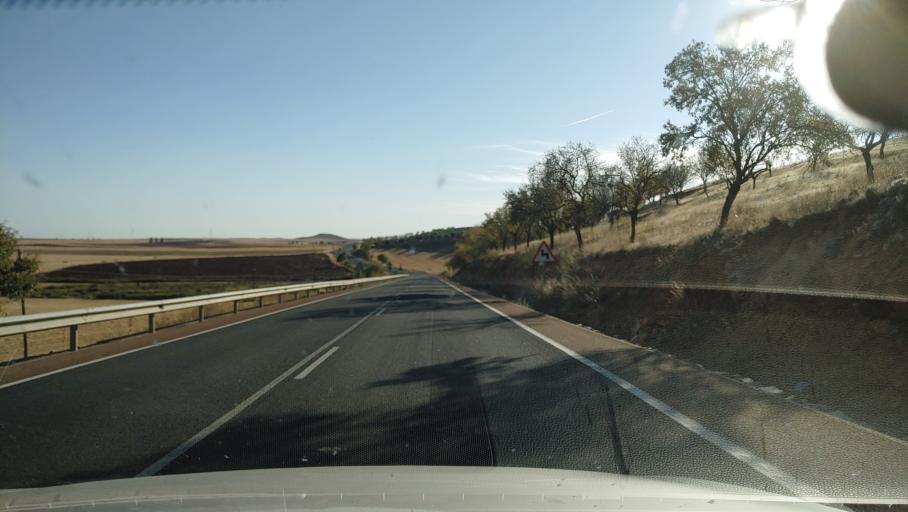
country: ES
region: Castille-La Mancha
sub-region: Provincia de Ciudad Real
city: Fuenllana
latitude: 38.7673
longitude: -2.9292
